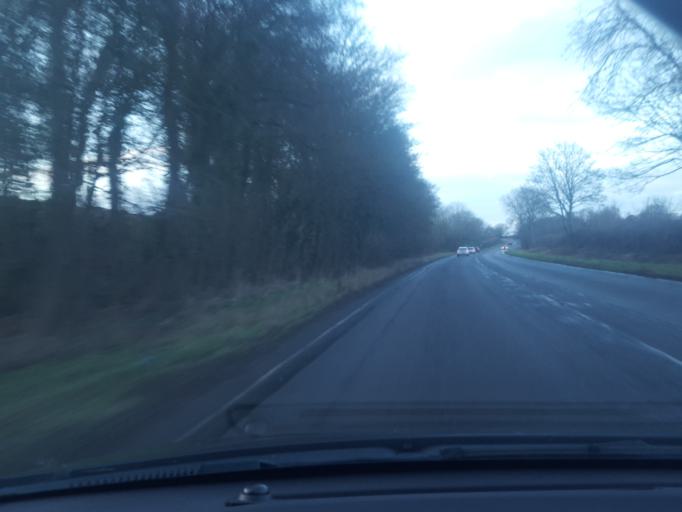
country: GB
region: England
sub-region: Shropshire
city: Albrighton
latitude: 52.6395
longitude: -2.2716
